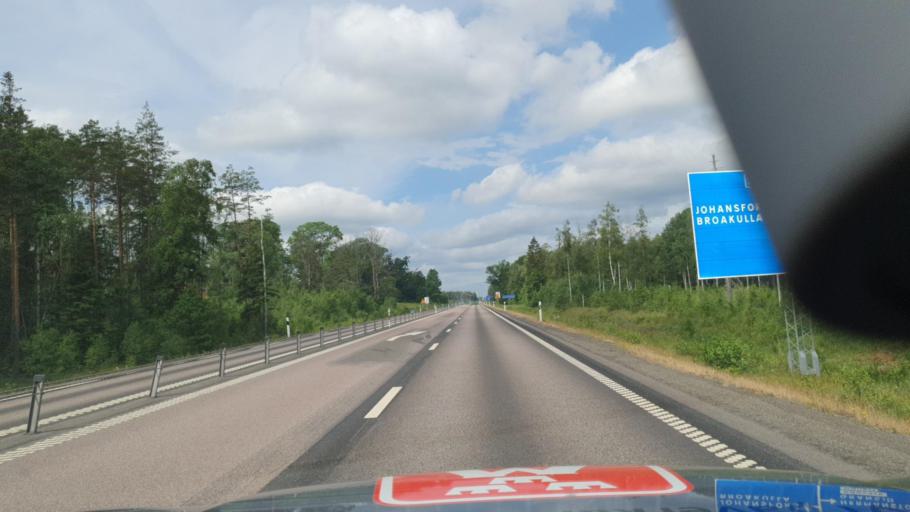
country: SE
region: Kalmar
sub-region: Emmaboda Kommun
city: Emmaboda
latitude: 56.7239
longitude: 15.5891
